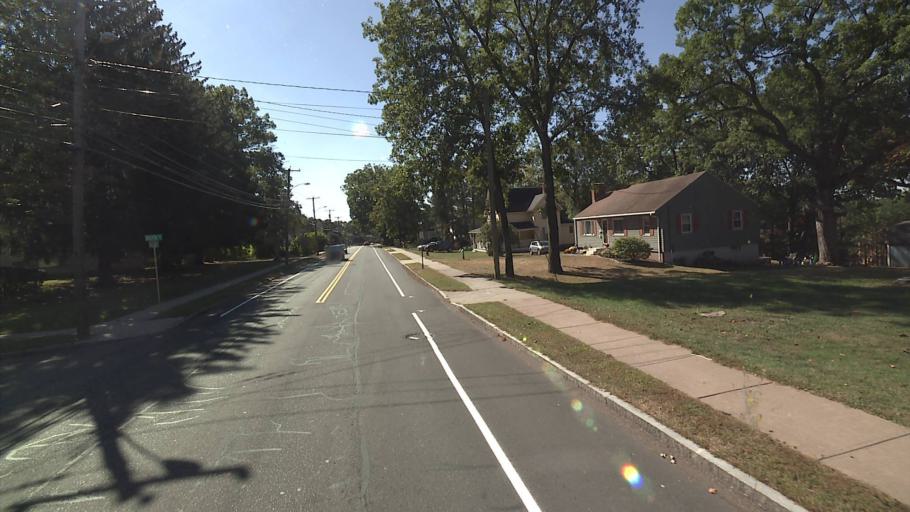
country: US
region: Connecticut
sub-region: Hartford County
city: Manchester
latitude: 41.8055
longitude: -72.5181
